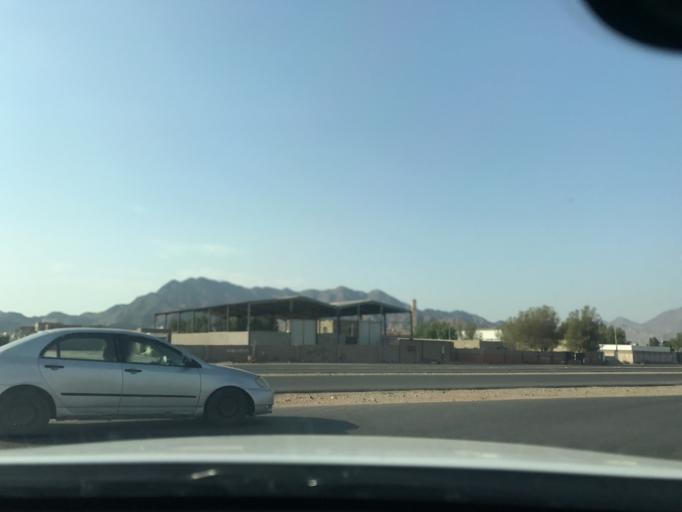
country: SA
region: Makkah
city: Al Jumum
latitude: 21.4416
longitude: 39.5155
